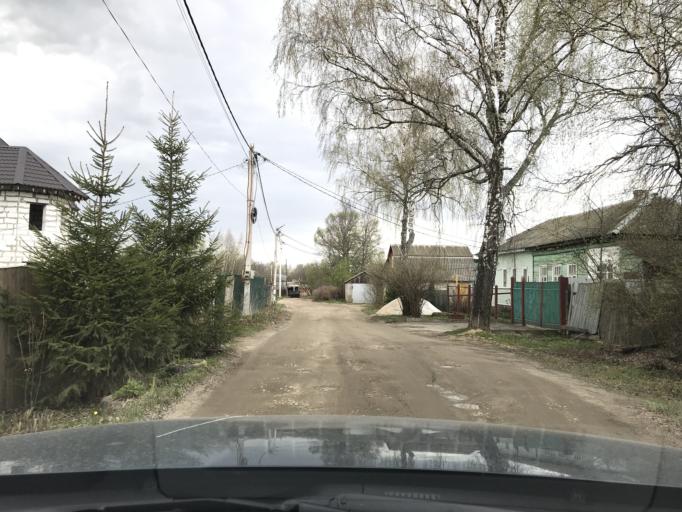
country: RU
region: Vladimir
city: Strunino
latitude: 56.3803
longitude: 38.5945
